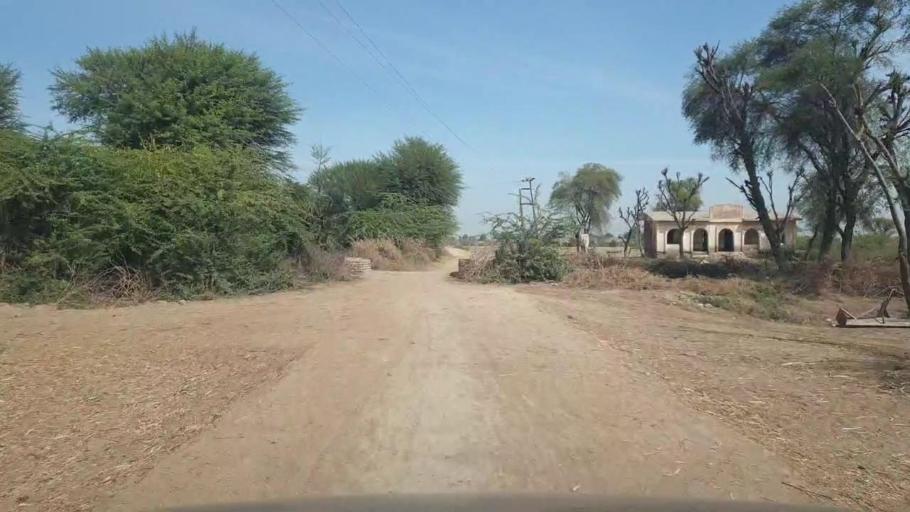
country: PK
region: Sindh
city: Umarkot
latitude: 25.3386
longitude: 69.6232
